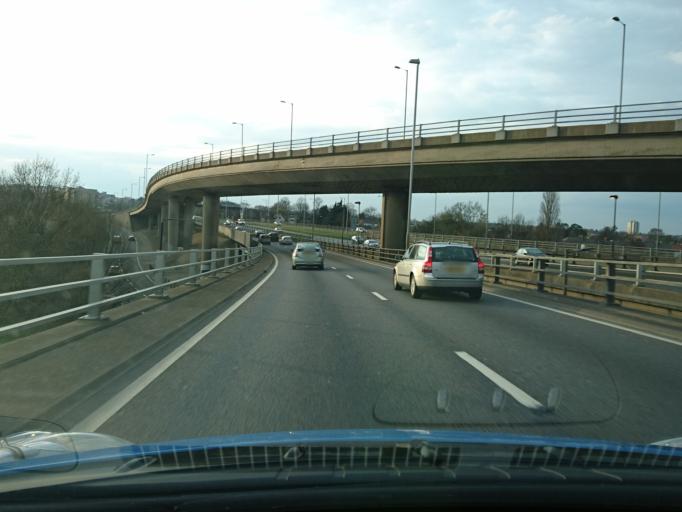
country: GB
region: England
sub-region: Greater London
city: Woodford Green
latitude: 51.5936
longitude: 0.0355
